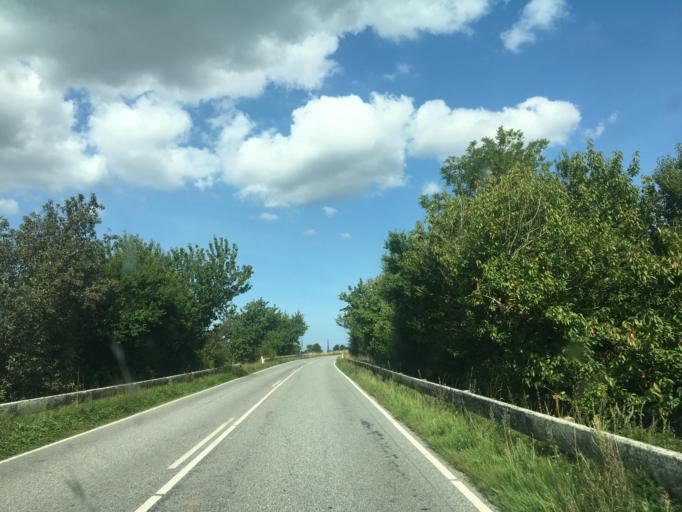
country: DK
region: South Denmark
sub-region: Middelfart Kommune
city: Ejby
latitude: 55.4108
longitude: 9.9155
